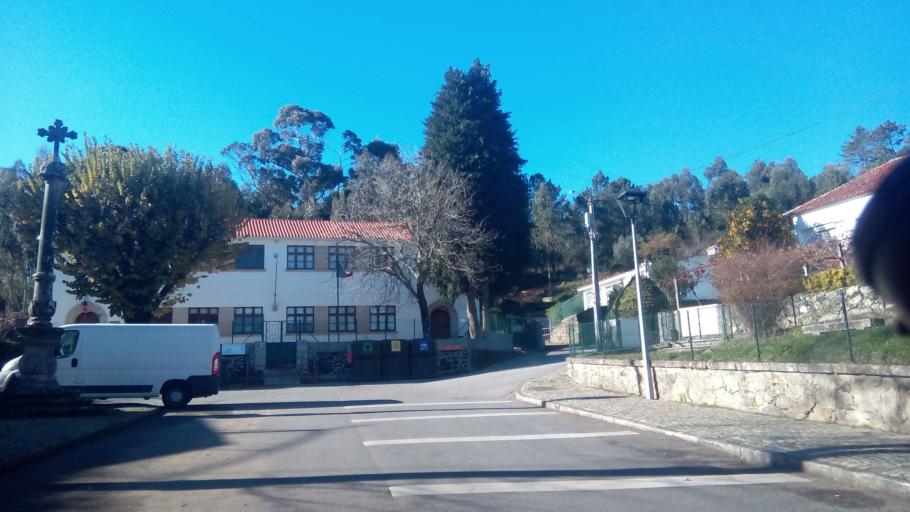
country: PT
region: Viana do Castelo
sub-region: Viana do Castelo
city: Darque
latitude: 41.7401
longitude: -8.7344
